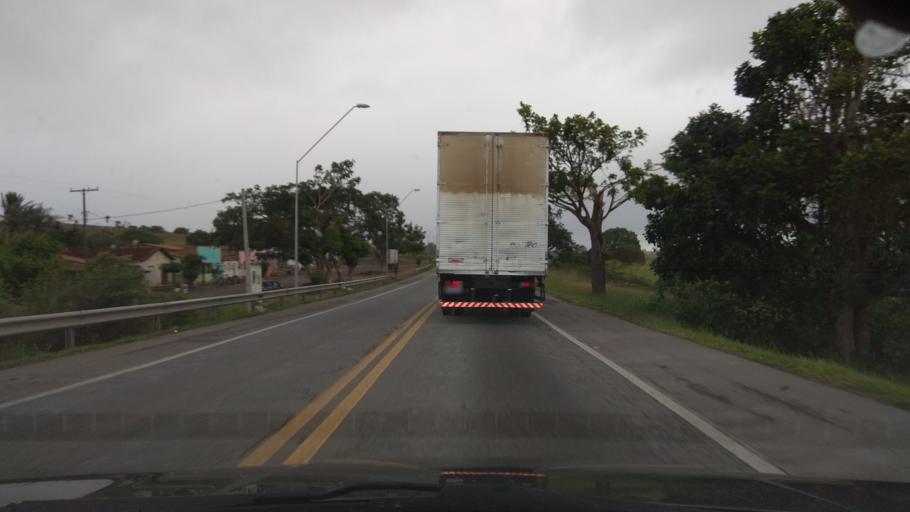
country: BR
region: Bahia
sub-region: Jaguaquara
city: Jaguaquara
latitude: -13.4812
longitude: -40.0424
